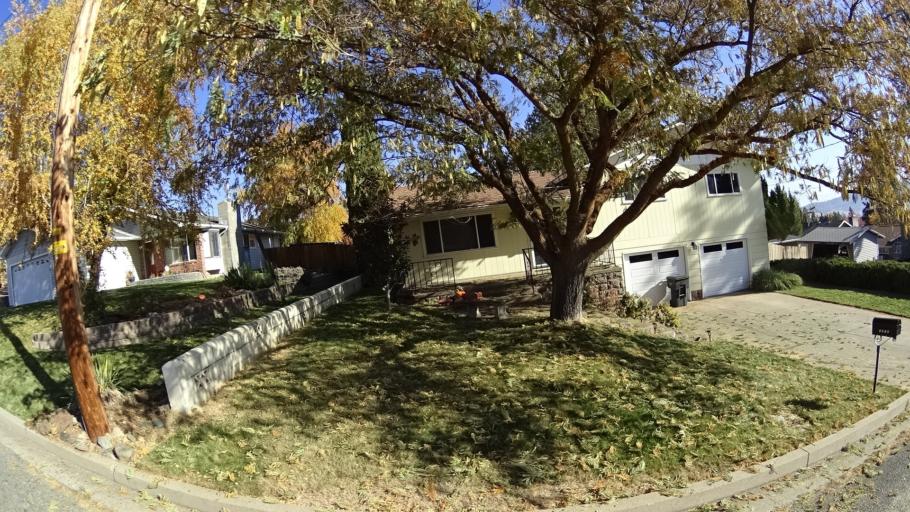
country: US
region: California
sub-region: Siskiyou County
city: Yreka
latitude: 41.7397
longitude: -122.6541
